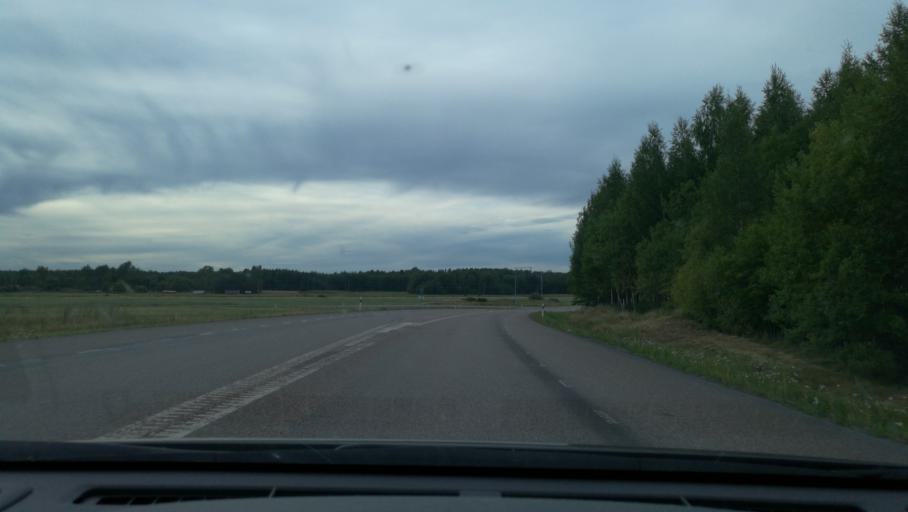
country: SE
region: Vaestmanland
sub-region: Kopings Kommun
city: Koping
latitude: 59.4820
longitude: 15.9857
